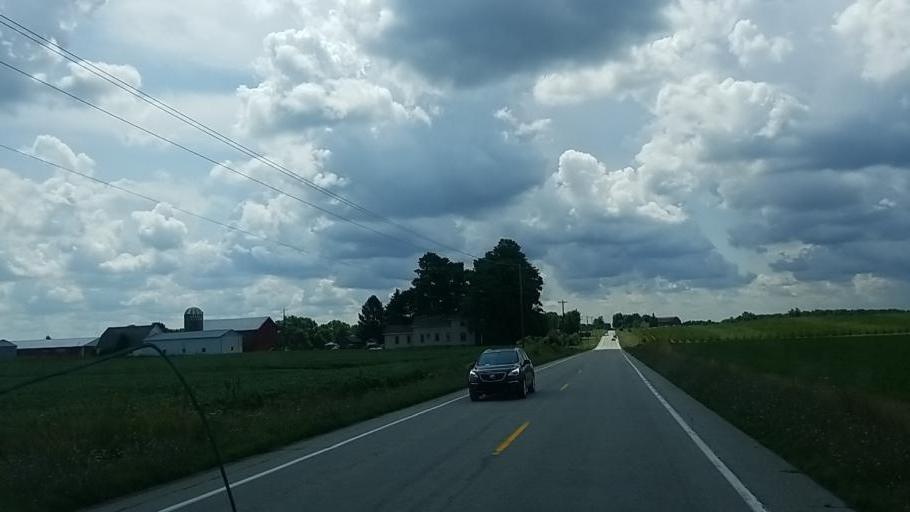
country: US
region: Michigan
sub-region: Kent County
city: Walker
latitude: 43.0809
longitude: -85.7681
